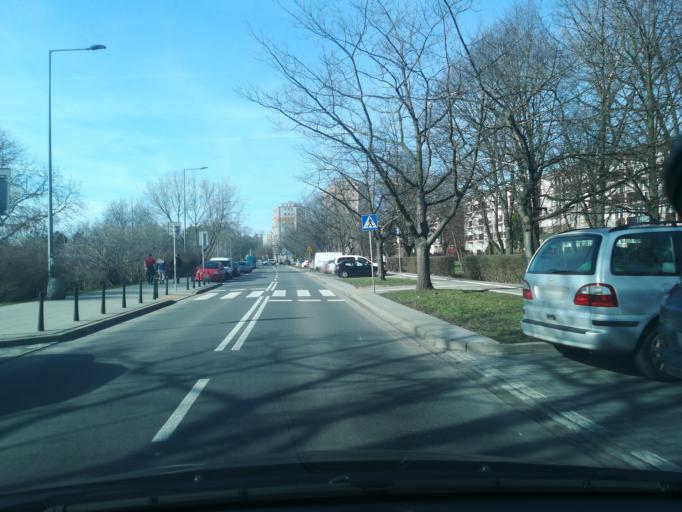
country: PL
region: Masovian Voivodeship
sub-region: Warszawa
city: Praga Poludnie
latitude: 52.2375
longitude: 21.0758
